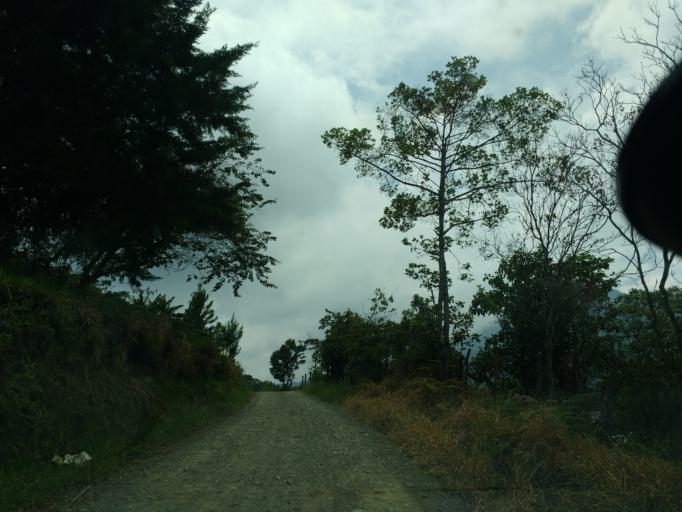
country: CO
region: Cauca
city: Santander de Quilichao
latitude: 2.9180
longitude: -76.4750
